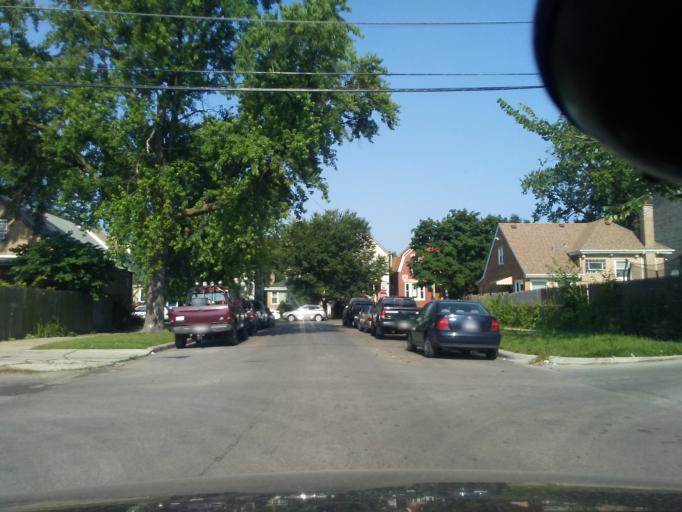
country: US
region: Illinois
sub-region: Cook County
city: Oak Park
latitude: 41.9203
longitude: -87.7688
